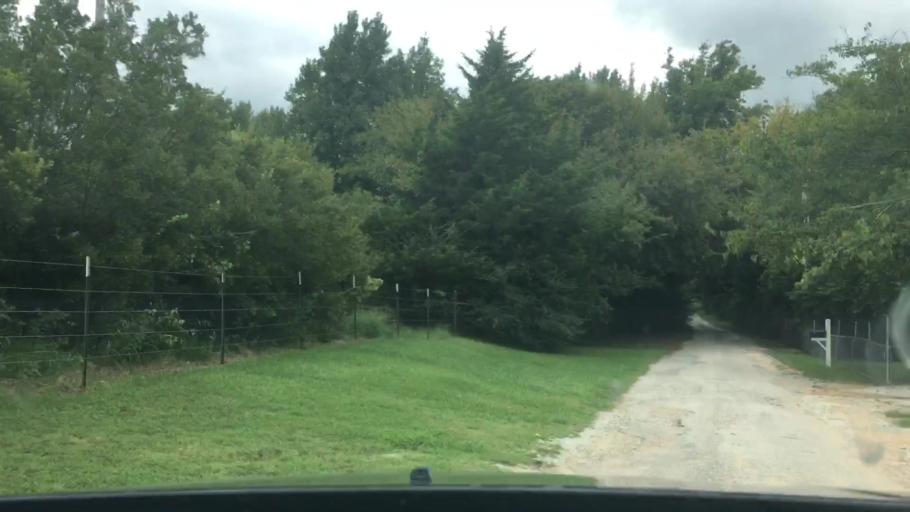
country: US
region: Oklahoma
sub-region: Pontotoc County
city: Ada
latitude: 34.7550
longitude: -96.6479
